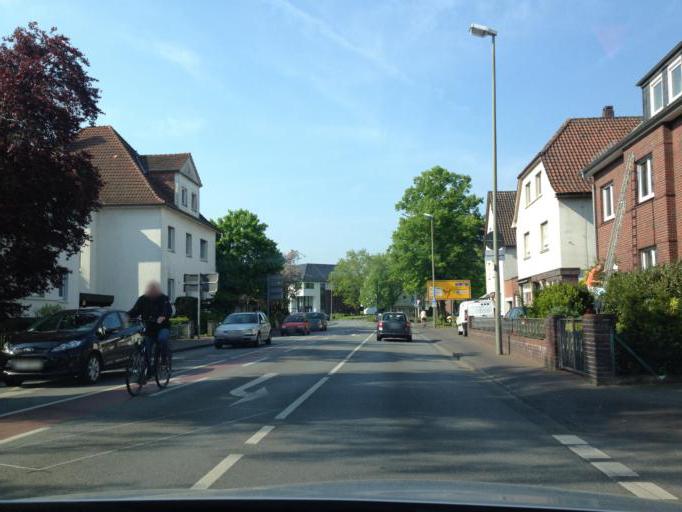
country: DE
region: North Rhine-Westphalia
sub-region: Regierungsbezirk Detmold
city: Guetersloh
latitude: 51.9012
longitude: 8.3789
